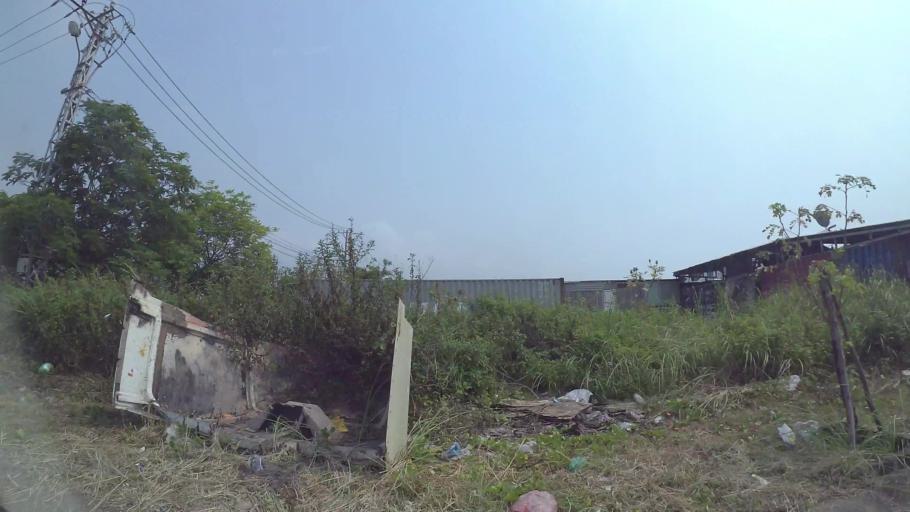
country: VN
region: Da Nang
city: Da Nang
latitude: 16.0923
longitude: 108.2370
